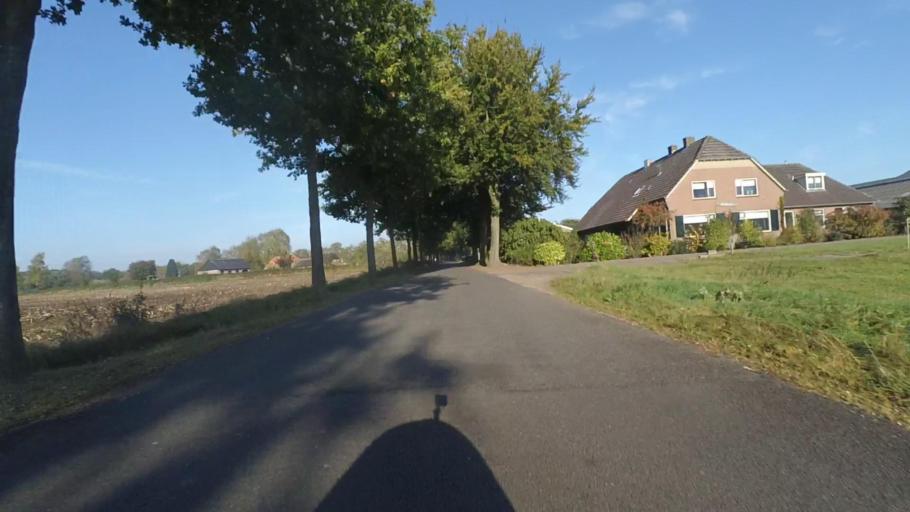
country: NL
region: Gelderland
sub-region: Gemeente Epe
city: Vaassen
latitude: 52.2937
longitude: 5.9548
